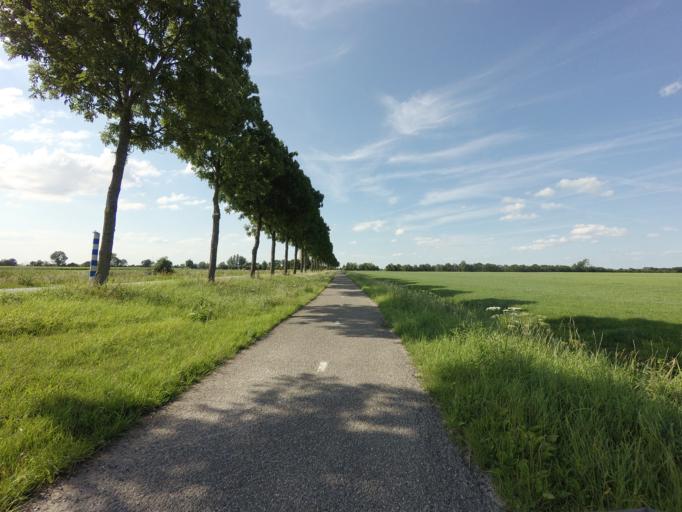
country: NL
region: Utrecht
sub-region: Gemeente Lopik
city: Lopik
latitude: 51.9821
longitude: 4.9134
